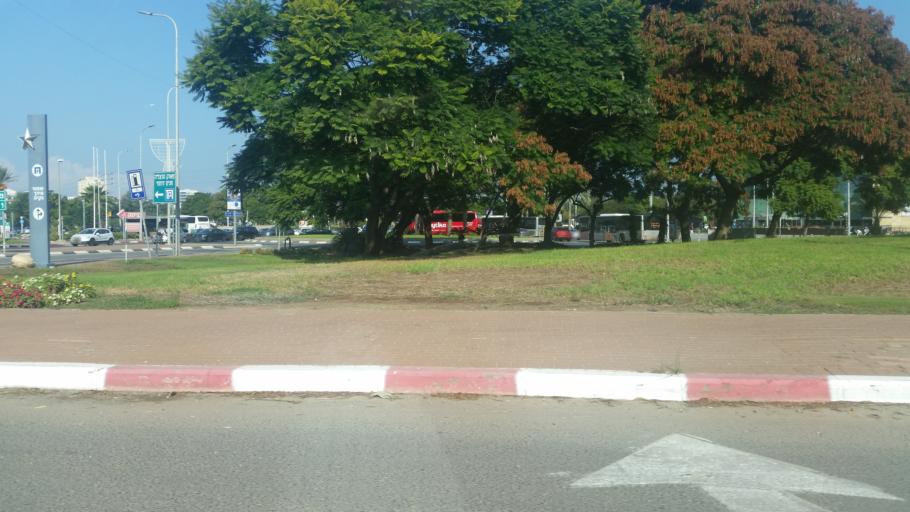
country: IL
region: Tel Aviv
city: Herzliyya
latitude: 32.1634
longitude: 34.8235
